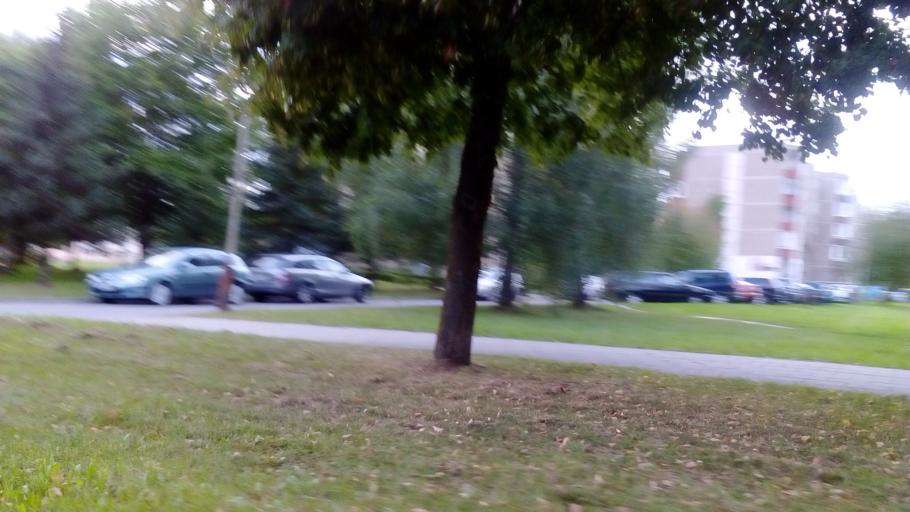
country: LT
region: Alytaus apskritis
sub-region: Alytus
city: Alytus
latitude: 54.3957
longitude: 24.0247
